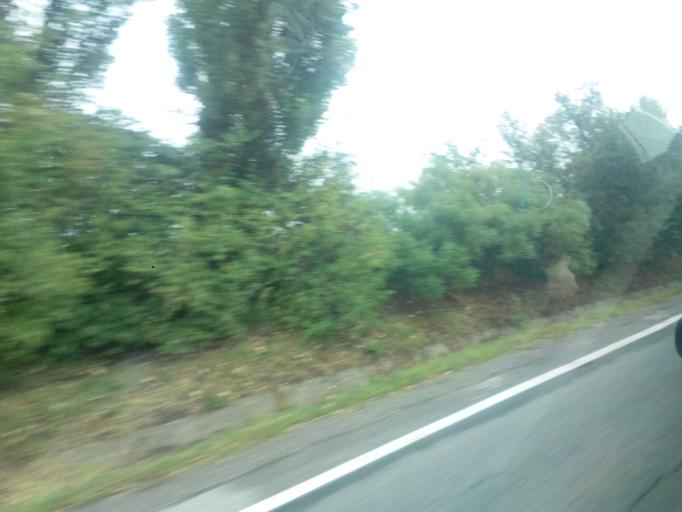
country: RO
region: Cluj
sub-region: Comuna Mihai Viteazu
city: Mihai Viteazu
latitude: 46.5347
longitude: 23.7208
